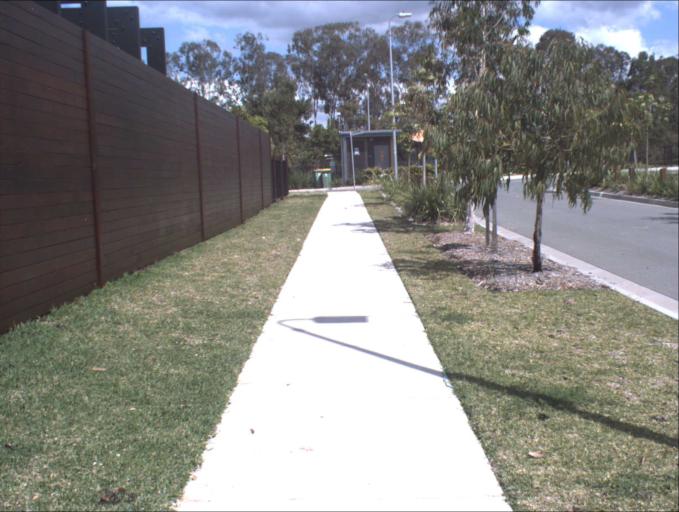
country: AU
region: Queensland
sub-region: Logan
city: Chambers Flat
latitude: -27.8014
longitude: 153.1056
